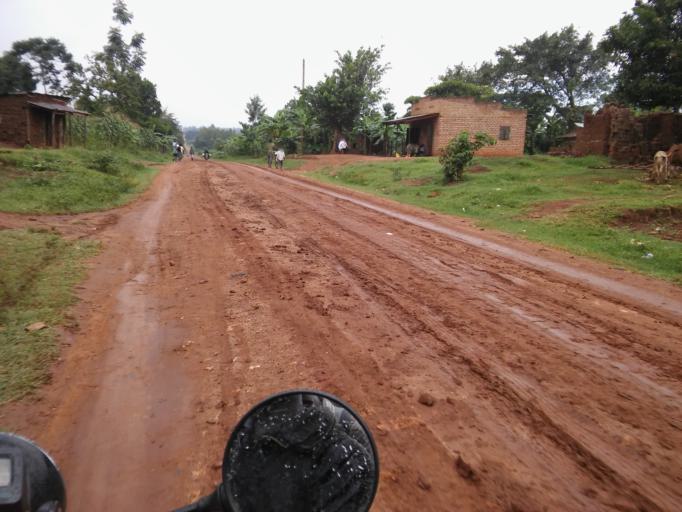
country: UG
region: Eastern Region
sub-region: Mbale District
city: Mbale
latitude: 1.0022
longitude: 34.1922
